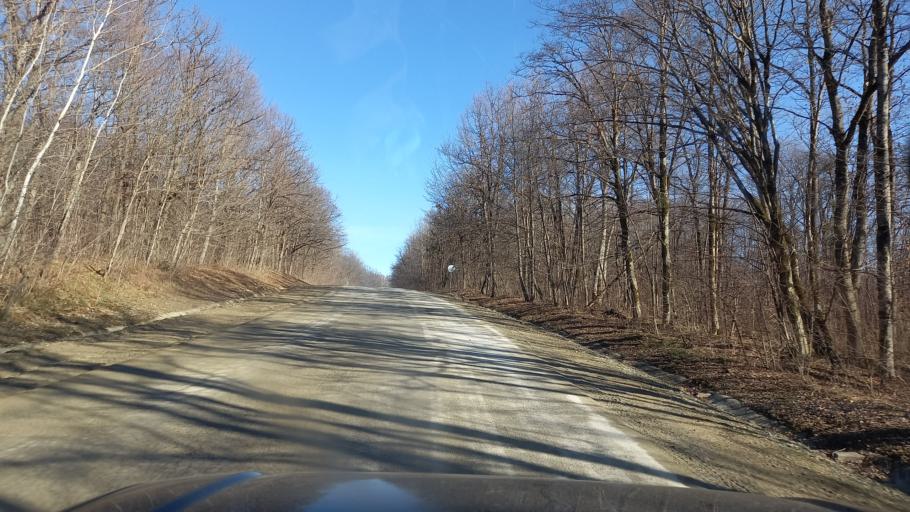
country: RU
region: Adygeya
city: Kamennomostskiy
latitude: 44.2810
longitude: 40.2592
